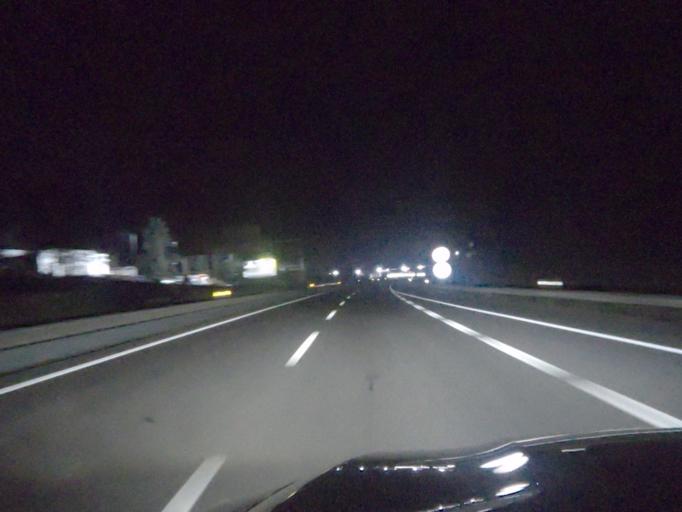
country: PT
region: Santarem
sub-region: Ourem
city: Fatima
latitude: 39.6270
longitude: -8.6968
